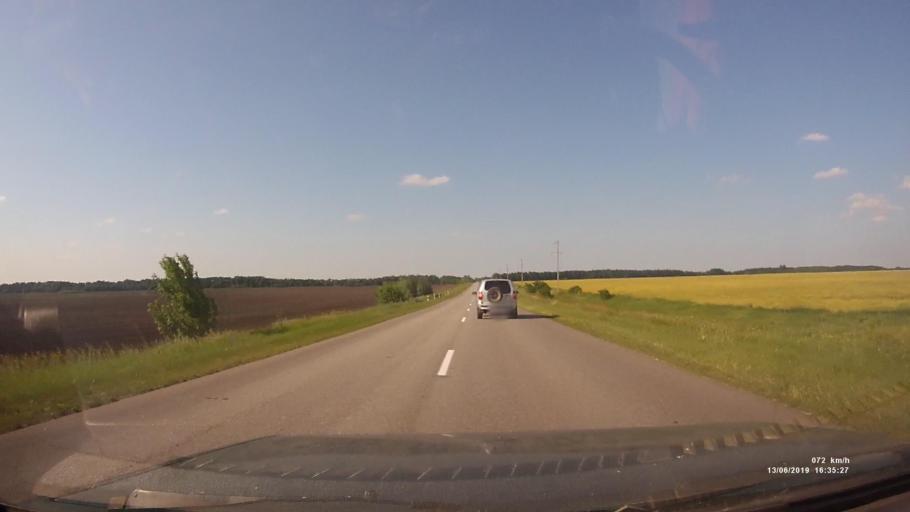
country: RU
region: Rostov
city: Kazanskaya
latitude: 49.8825
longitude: 41.2985
